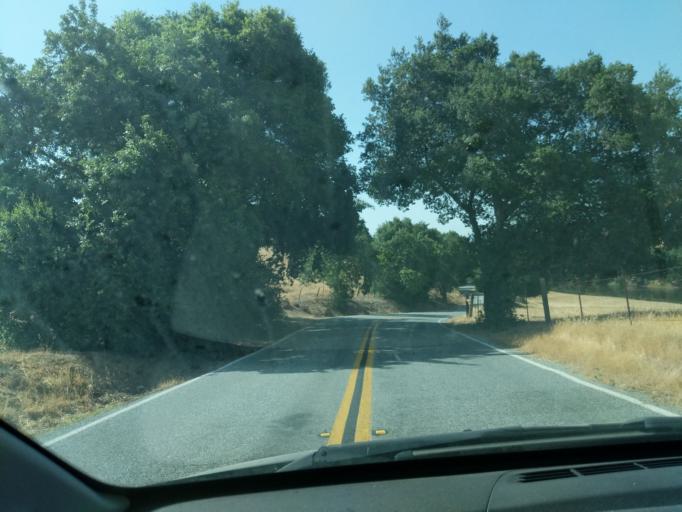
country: US
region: California
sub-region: Santa Clara County
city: Gilroy
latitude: 37.0654
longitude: -121.5222
